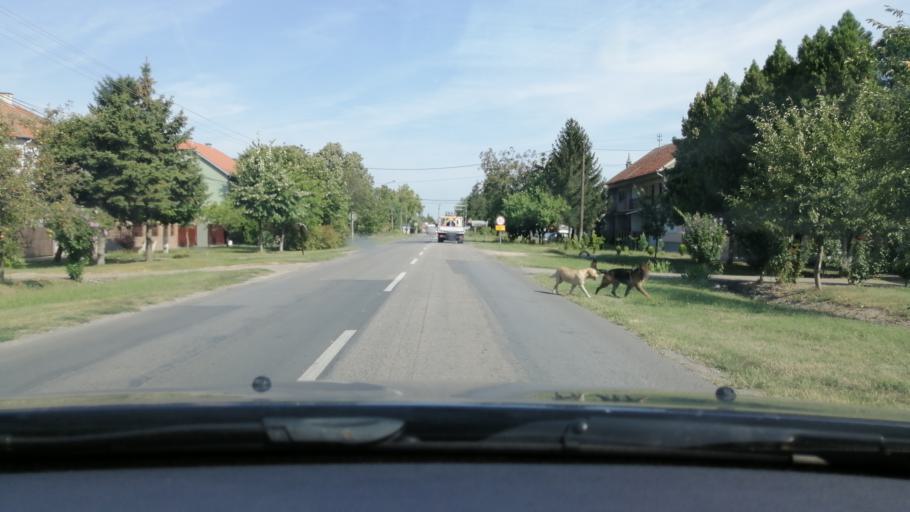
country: RS
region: Autonomna Pokrajina Vojvodina
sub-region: Juznobanatski Okrug
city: Kovacica
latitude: 45.1090
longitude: 20.6192
